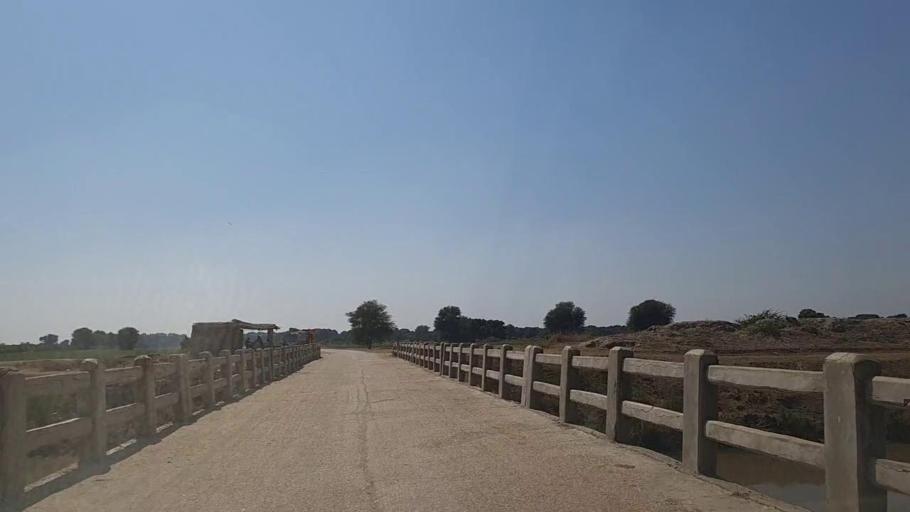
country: PK
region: Sindh
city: Samaro
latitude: 25.3479
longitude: 69.3122
